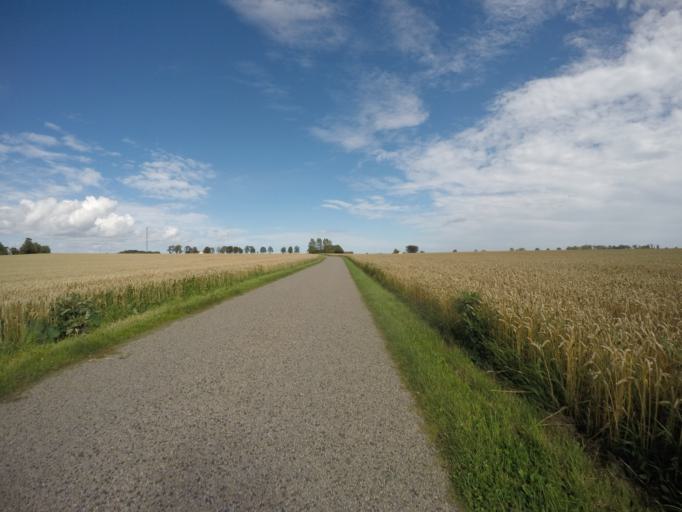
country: SE
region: Skane
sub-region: Simrishamns Kommun
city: Simrishamn
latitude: 55.4932
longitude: 14.2499
